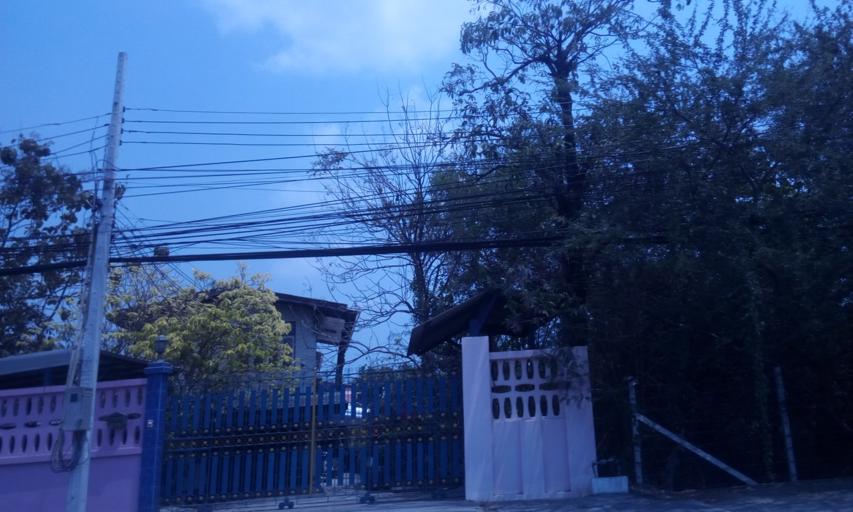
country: TH
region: Chachoengsao
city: Chachoengsao
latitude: 13.7045
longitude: 101.0915
